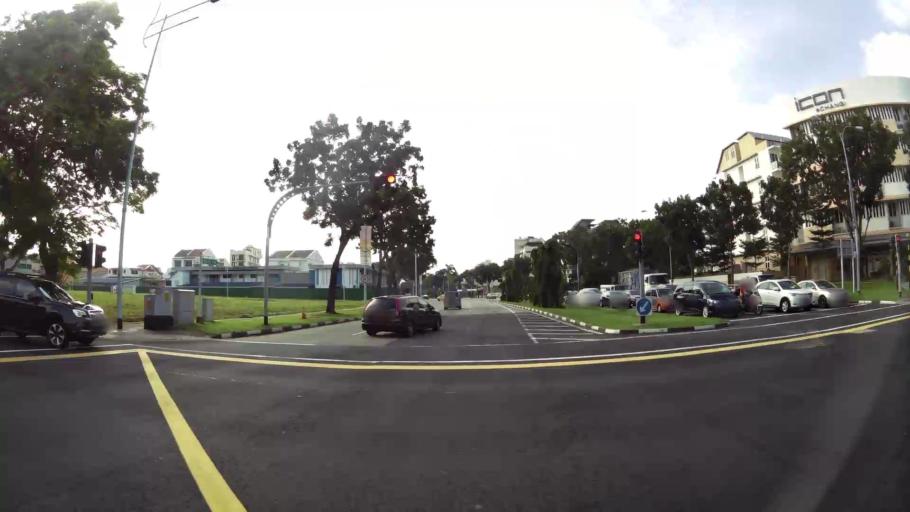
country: SG
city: Singapore
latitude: 1.3176
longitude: 103.9050
